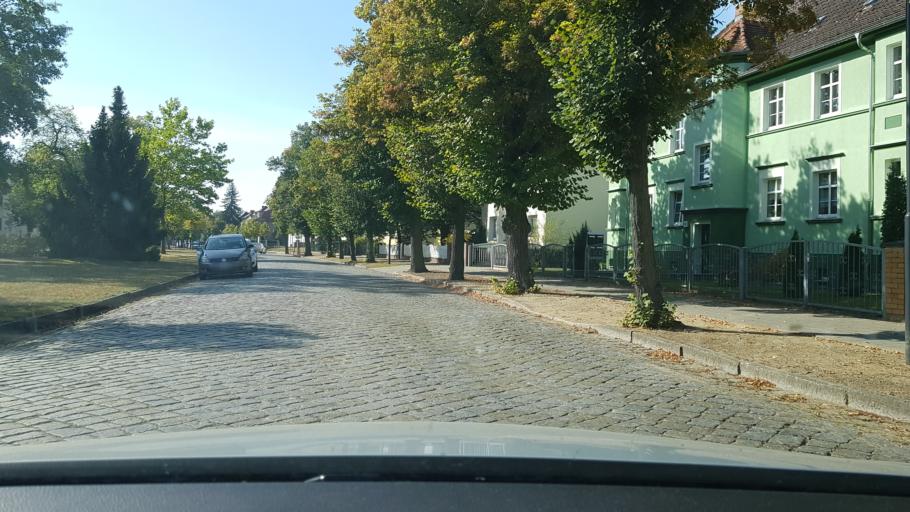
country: DE
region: Brandenburg
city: Beeskow
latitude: 52.1713
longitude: 14.2398
